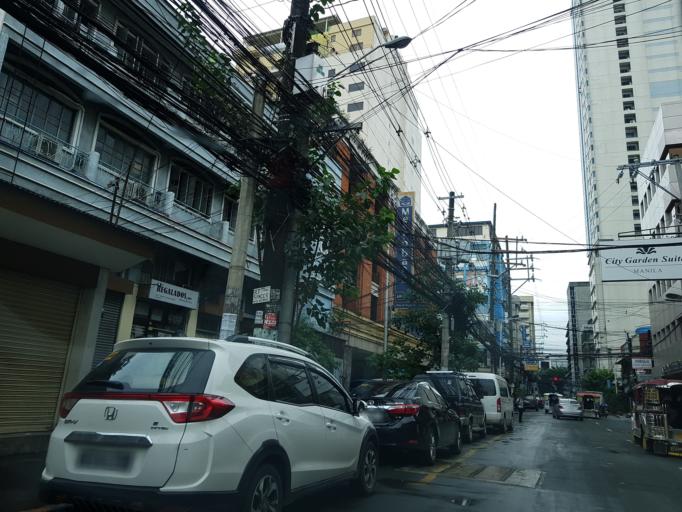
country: PH
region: Metro Manila
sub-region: City of Manila
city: Port Area
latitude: 14.5787
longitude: 120.9807
